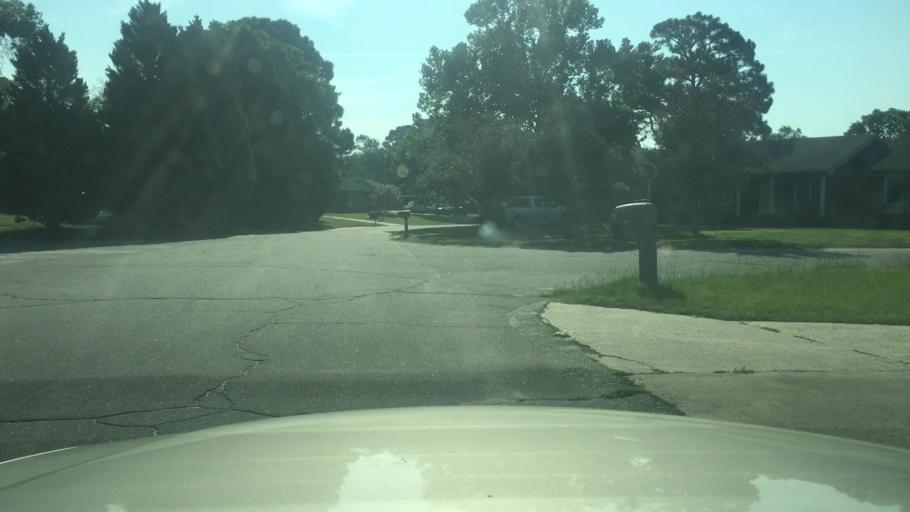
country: US
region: North Carolina
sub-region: Cumberland County
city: Spring Lake
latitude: 35.1585
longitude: -78.9071
